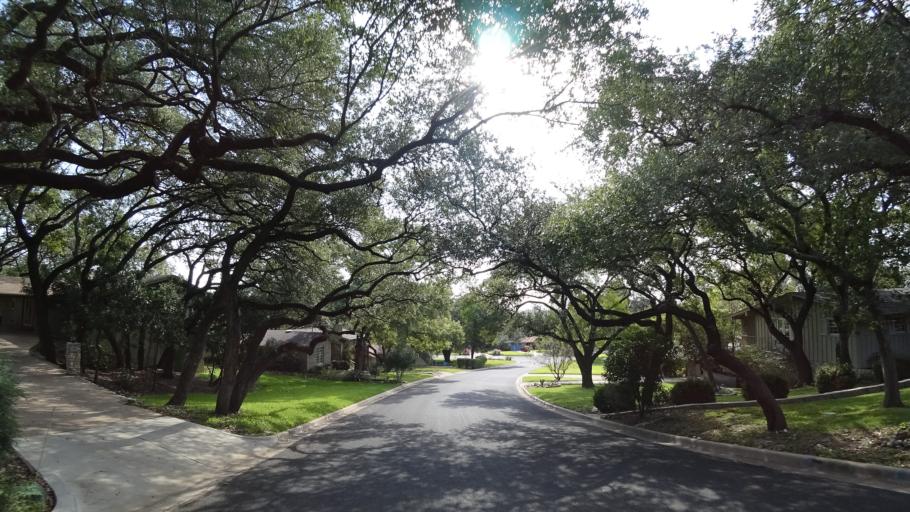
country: US
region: Texas
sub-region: Travis County
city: West Lake Hills
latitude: 30.3408
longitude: -97.7573
